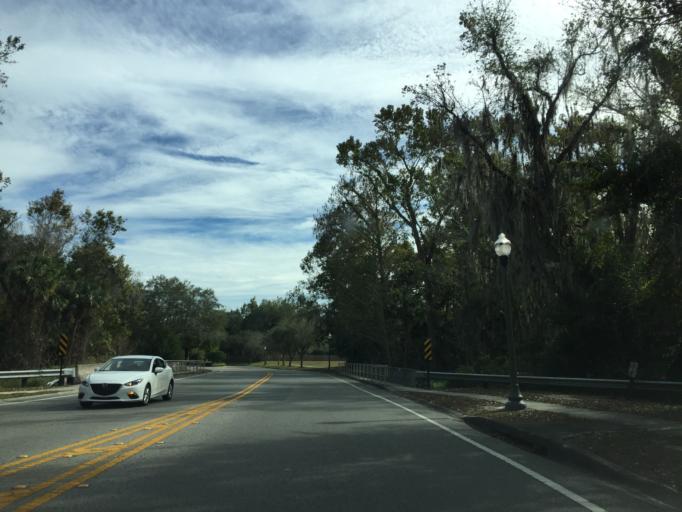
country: US
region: Florida
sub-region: Seminole County
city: Oviedo
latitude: 28.6687
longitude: -81.2337
